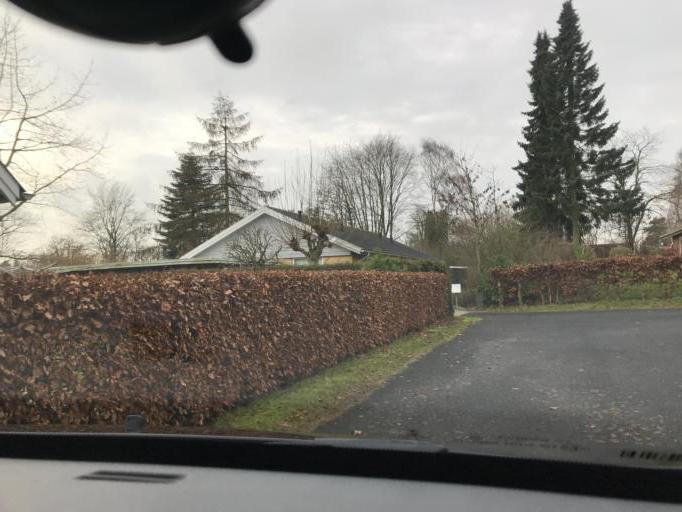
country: DK
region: South Denmark
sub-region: Faaborg-Midtfyn Kommune
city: Ringe
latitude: 55.2446
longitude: 10.4723
